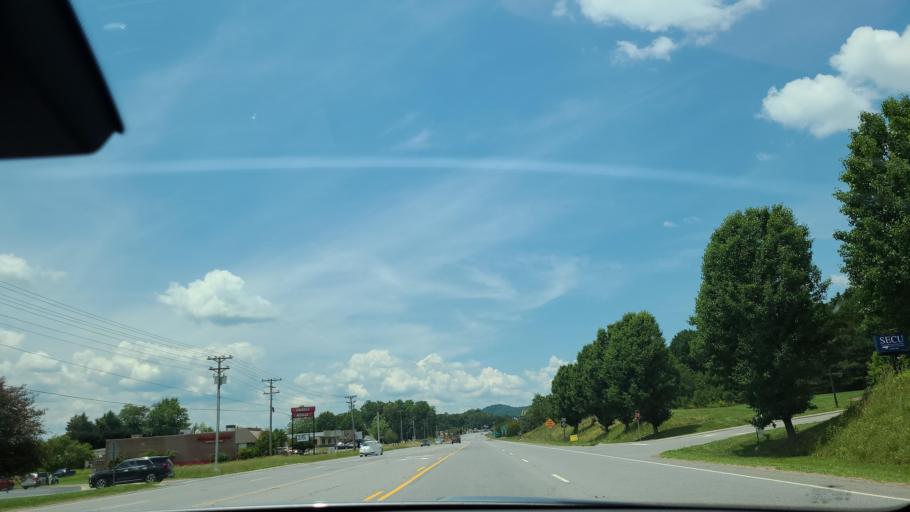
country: US
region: North Carolina
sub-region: Clay County
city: Hayesville
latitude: 35.0346
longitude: -83.8159
